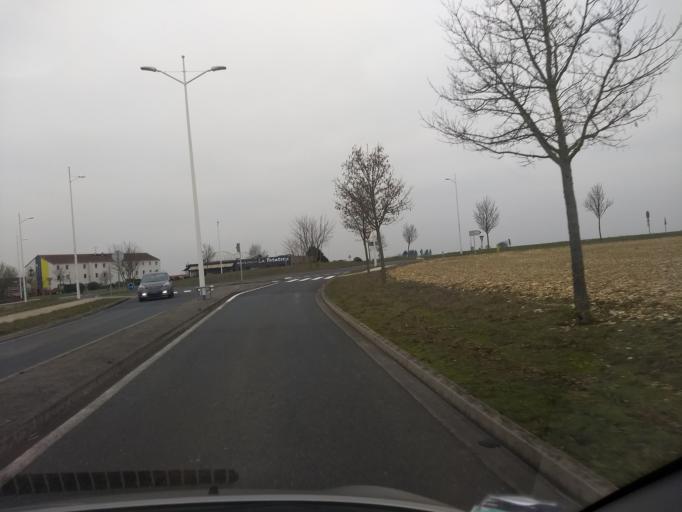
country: FR
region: Centre
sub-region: Departement de l'Indre
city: Deols
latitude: 46.8513
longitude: 1.7068
